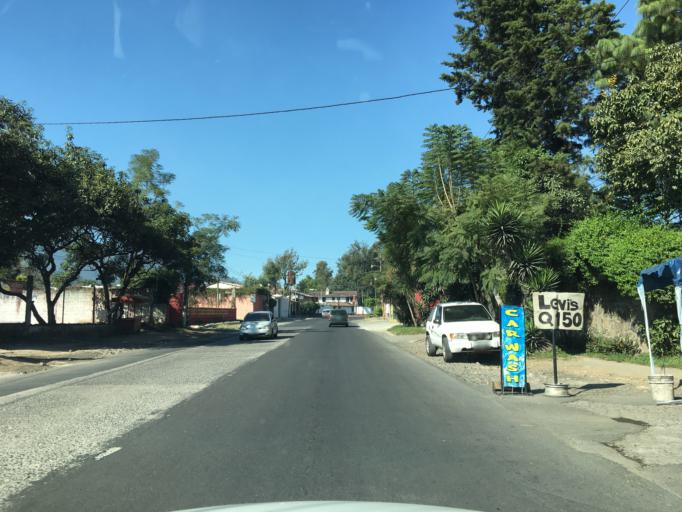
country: GT
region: Sacatepequez
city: Antigua Guatemala
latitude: 14.5448
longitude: -90.7467
